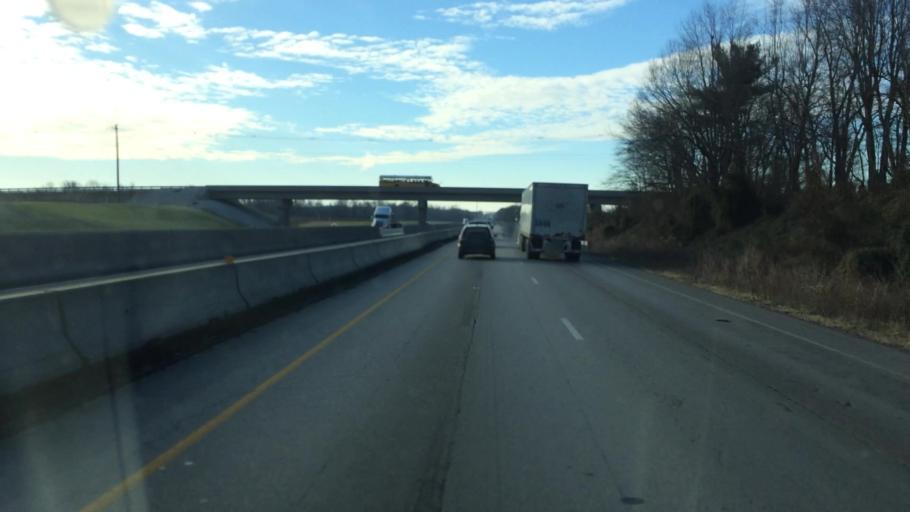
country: US
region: Kentucky
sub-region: Hardin County
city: Elizabethtown
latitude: 37.5750
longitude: -85.8735
